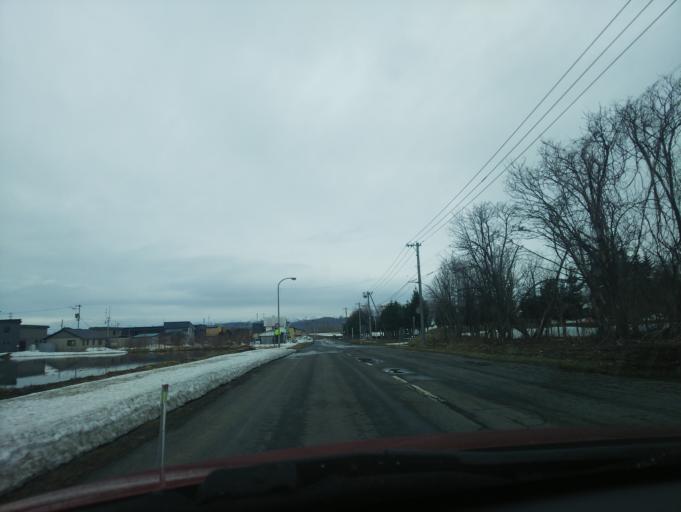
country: JP
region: Hokkaido
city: Nayoro
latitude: 44.3664
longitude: 142.4532
